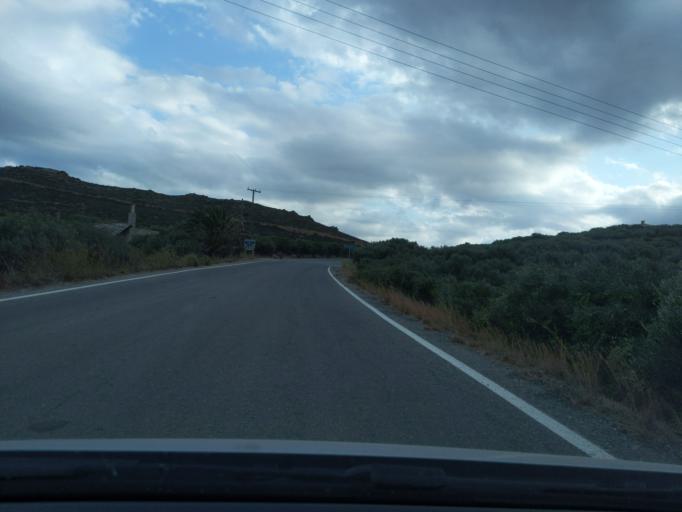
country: GR
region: Crete
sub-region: Nomos Lasithiou
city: Palekastro
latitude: 35.2220
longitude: 26.2590
